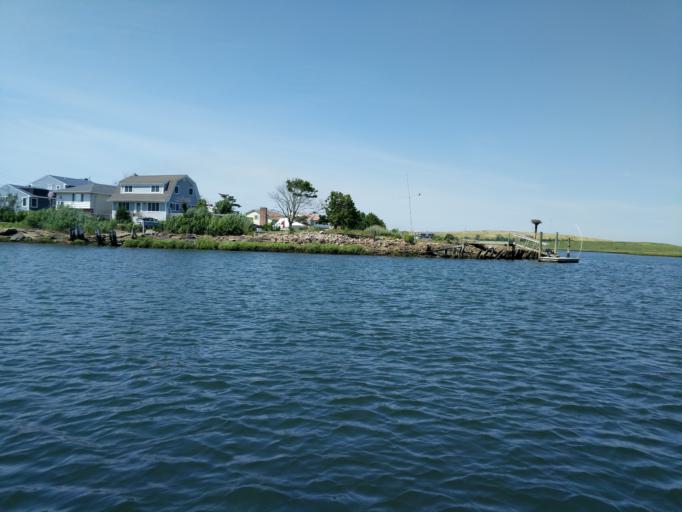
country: US
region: New York
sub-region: Nassau County
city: Barnum Island
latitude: 40.6040
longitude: -73.6430
